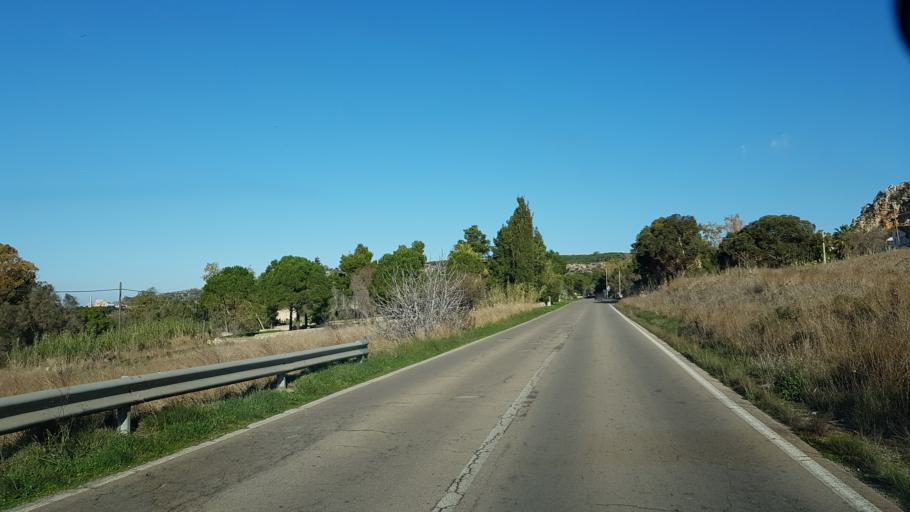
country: IT
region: Apulia
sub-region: Provincia di Lecce
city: Sannicola
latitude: 40.0995
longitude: 18.0199
